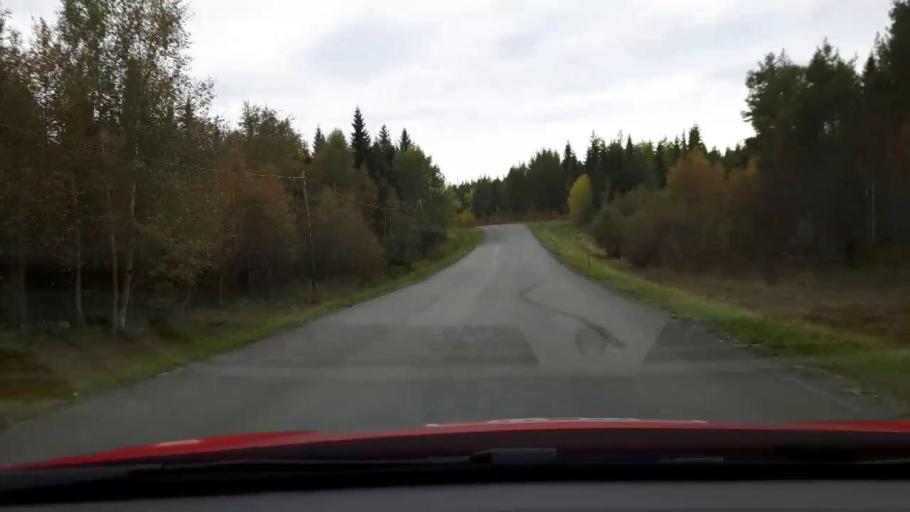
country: SE
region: Jaemtland
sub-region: Krokoms Kommun
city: Krokom
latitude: 63.2217
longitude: 14.1308
